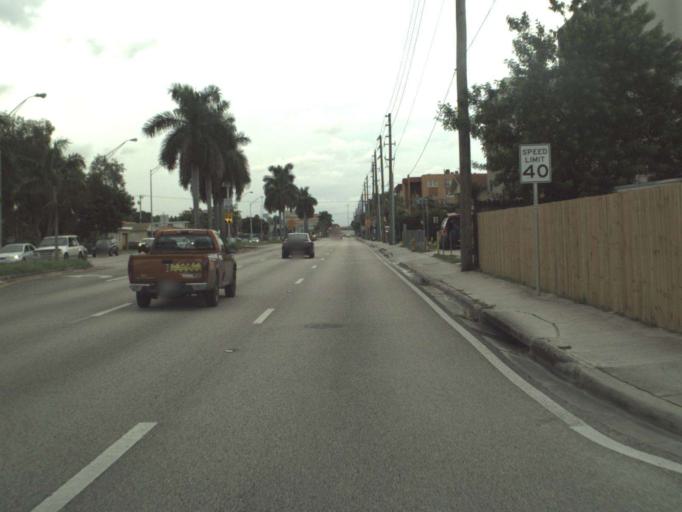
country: US
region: Florida
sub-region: Miami-Dade County
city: Flagami
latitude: 25.7716
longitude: -80.3121
